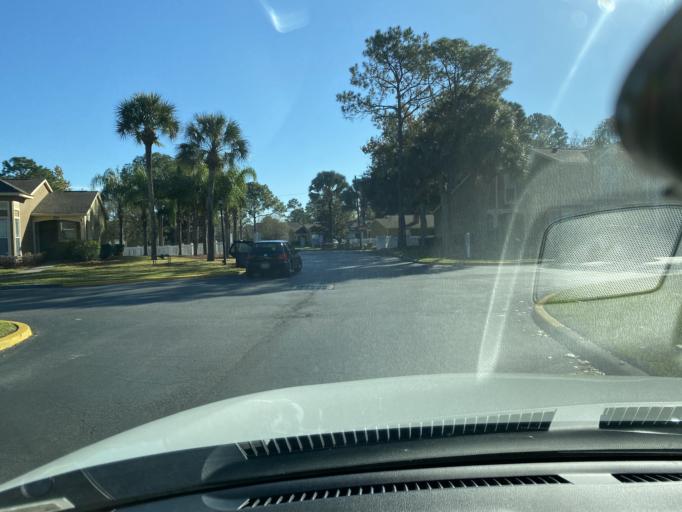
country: US
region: Florida
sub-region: Orange County
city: Azalea Park
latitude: 28.5182
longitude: -81.3068
